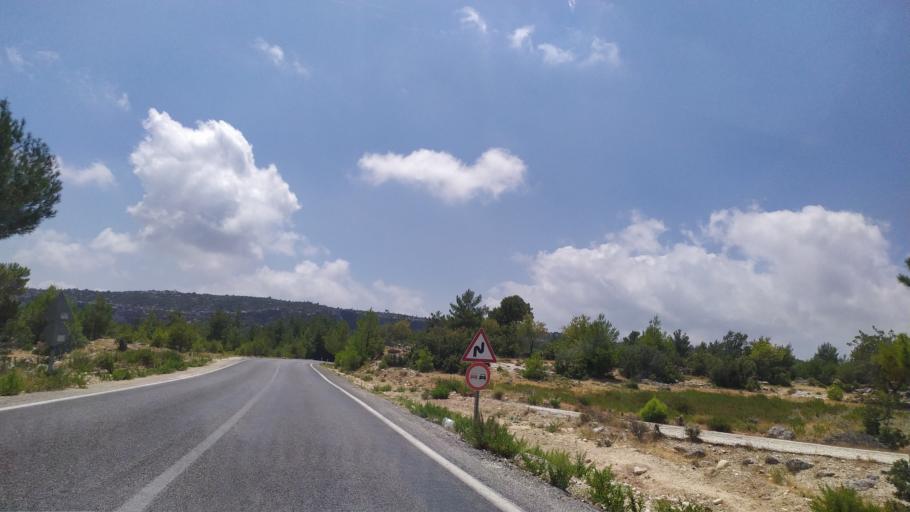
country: TR
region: Mersin
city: Gulnar
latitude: 36.2789
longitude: 33.3887
